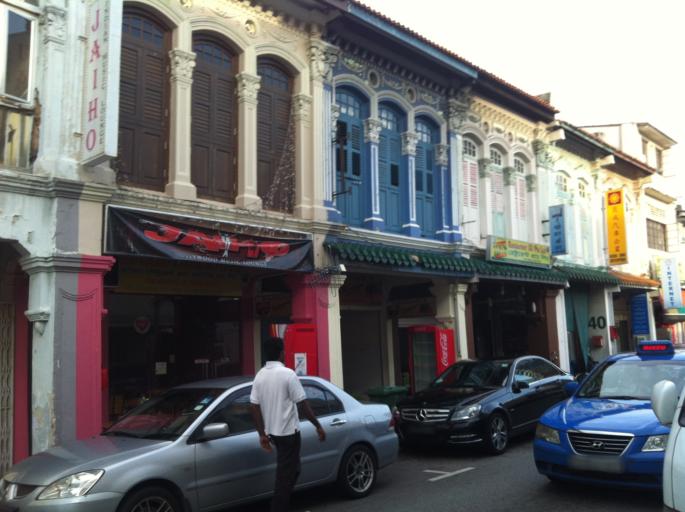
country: SG
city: Singapore
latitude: 1.3049
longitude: 103.8537
